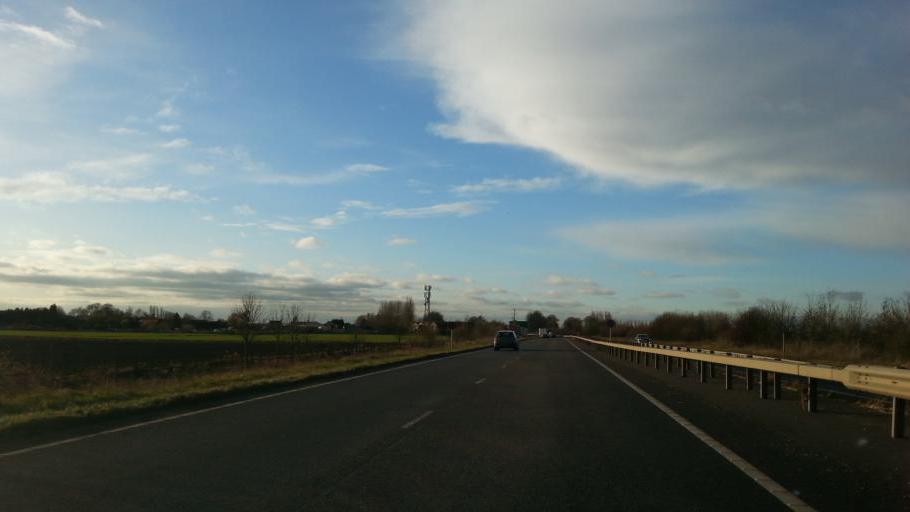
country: GB
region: England
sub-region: Peterborough
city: Thorney
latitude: 52.6263
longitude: -0.0993
